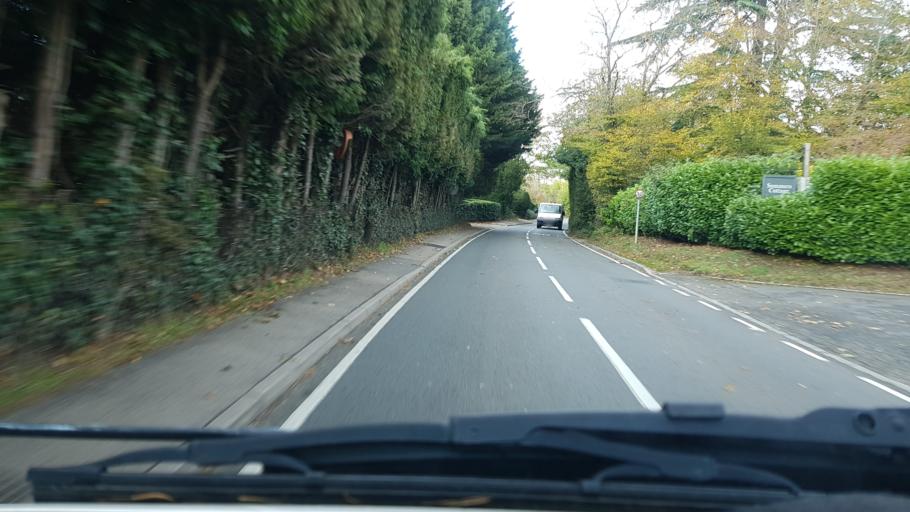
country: GB
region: England
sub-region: Surrey
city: Send
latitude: 51.2581
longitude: -0.5033
